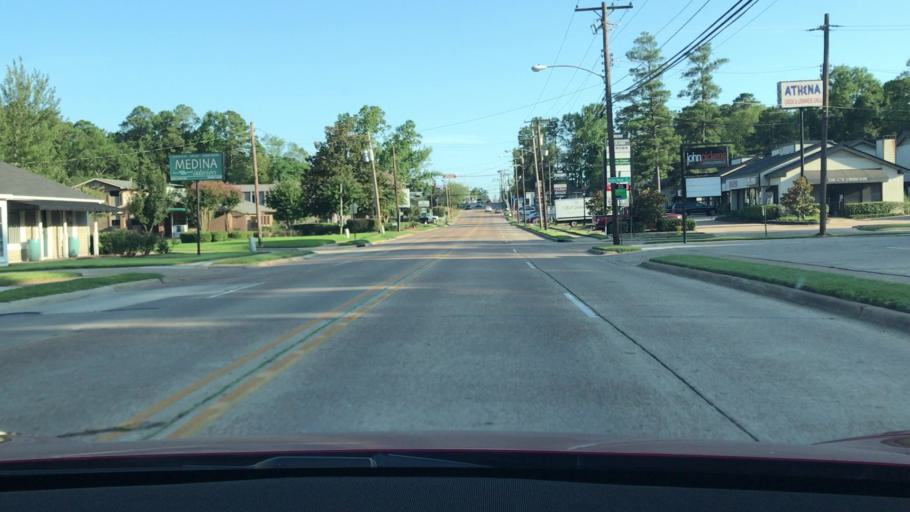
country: US
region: Louisiana
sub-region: Bossier Parish
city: Bossier City
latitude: 32.4525
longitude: -93.7461
